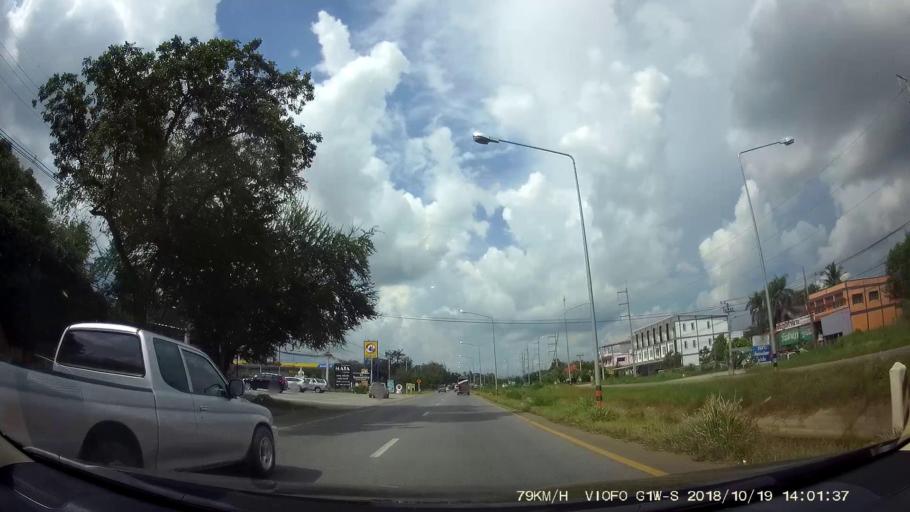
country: TH
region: Chaiyaphum
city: Chaiyaphum
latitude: 15.8313
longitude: 102.0585
